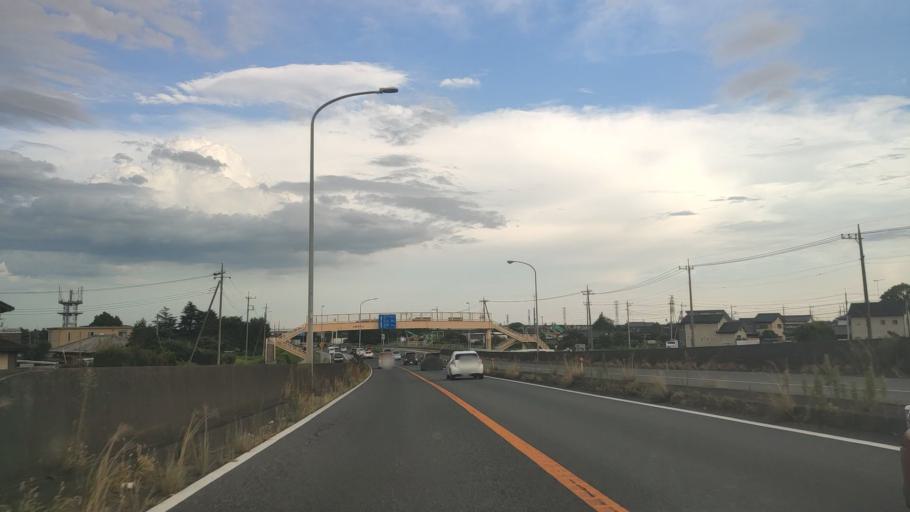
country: JP
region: Gunma
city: Ota
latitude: 36.3365
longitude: 139.3894
